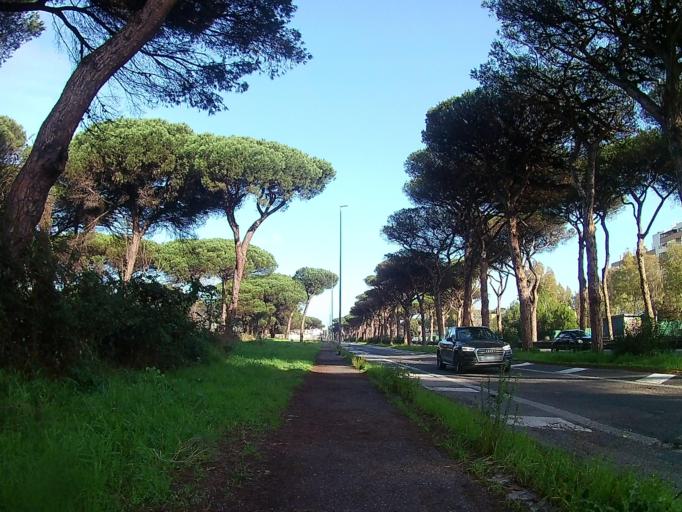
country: IT
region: Latium
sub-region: Citta metropolitana di Roma Capitale
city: Lido di Ostia
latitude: 41.7423
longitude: 12.2853
